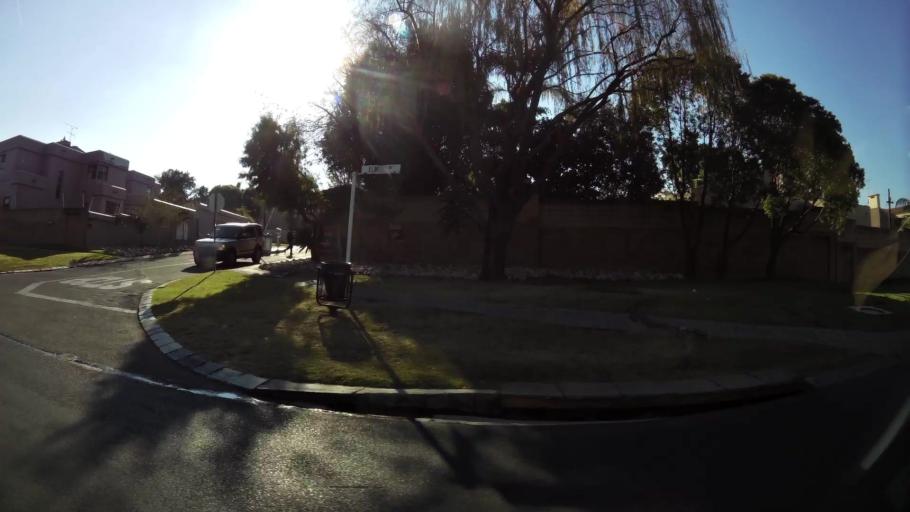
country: ZA
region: Gauteng
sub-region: City of Johannesburg Metropolitan Municipality
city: Modderfontein
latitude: -26.1432
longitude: 28.1383
